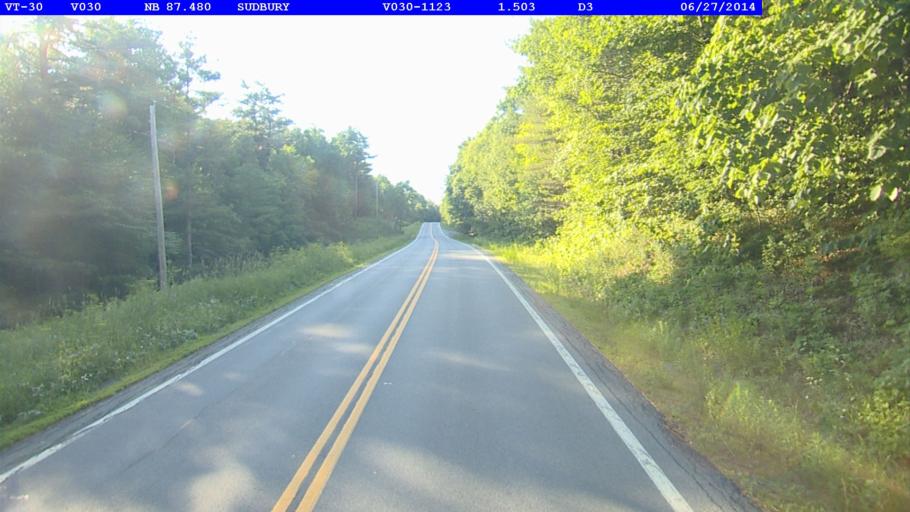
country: US
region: Vermont
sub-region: Rutland County
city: Brandon
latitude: 43.7705
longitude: -73.1992
